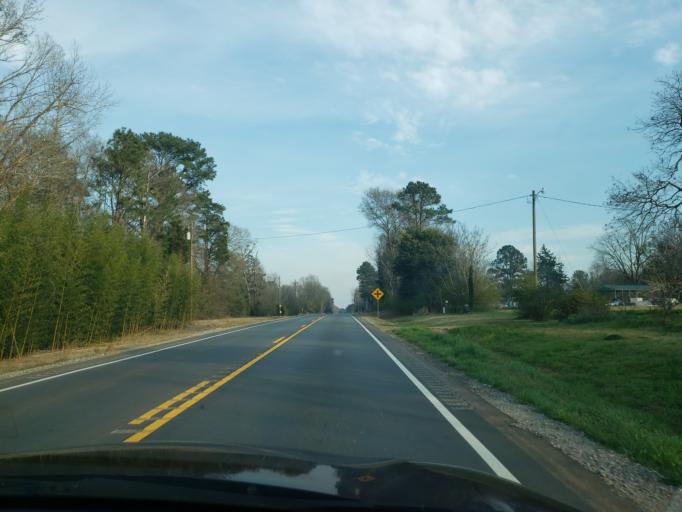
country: US
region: Alabama
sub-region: Hale County
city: Moundville
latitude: 32.8961
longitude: -87.6217
